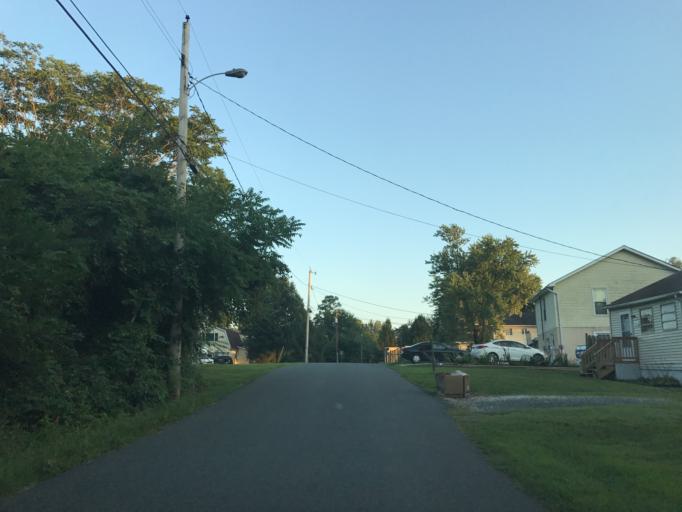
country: US
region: Maryland
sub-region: Baltimore County
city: Edgemere
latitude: 39.2790
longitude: -76.4369
